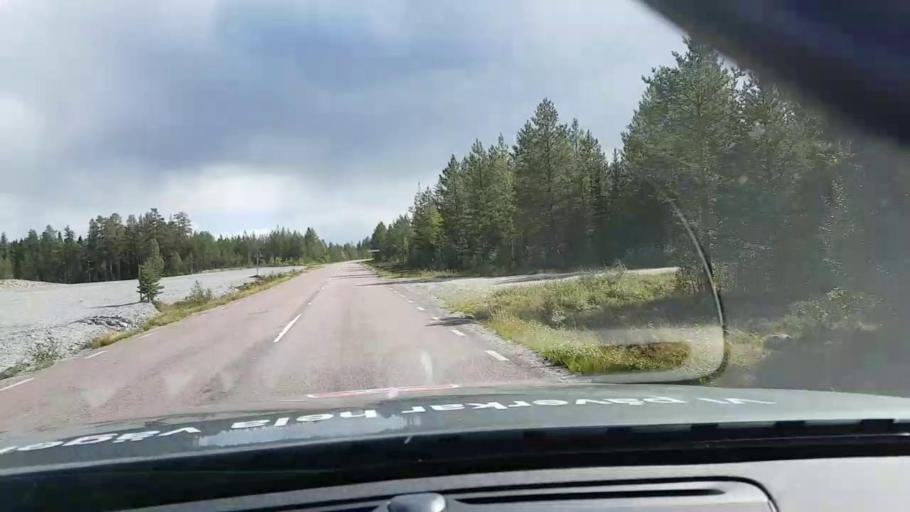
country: SE
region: Vaesterbotten
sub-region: Asele Kommun
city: Asele
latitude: 63.8882
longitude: 17.3496
